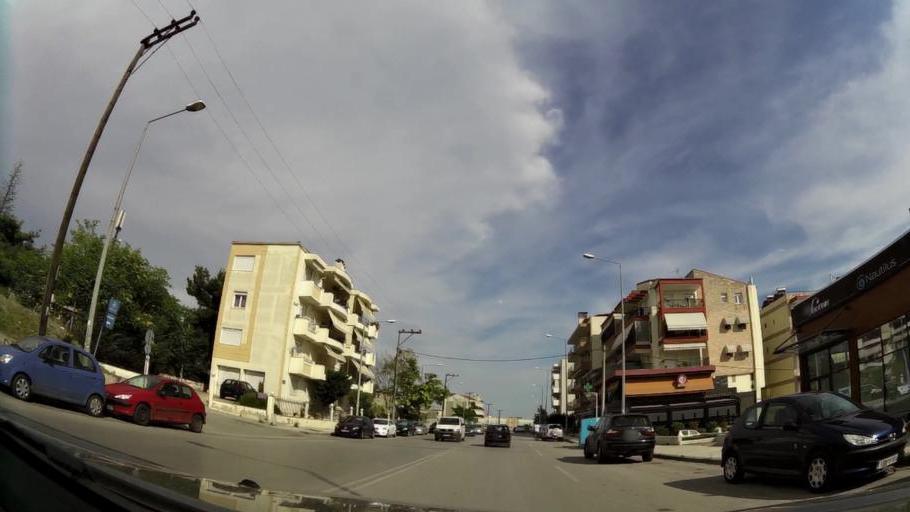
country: GR
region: Central Macedonia
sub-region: Nomos Thessalonikis
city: Kalamaria
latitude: 40.5767
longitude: 22.9654
